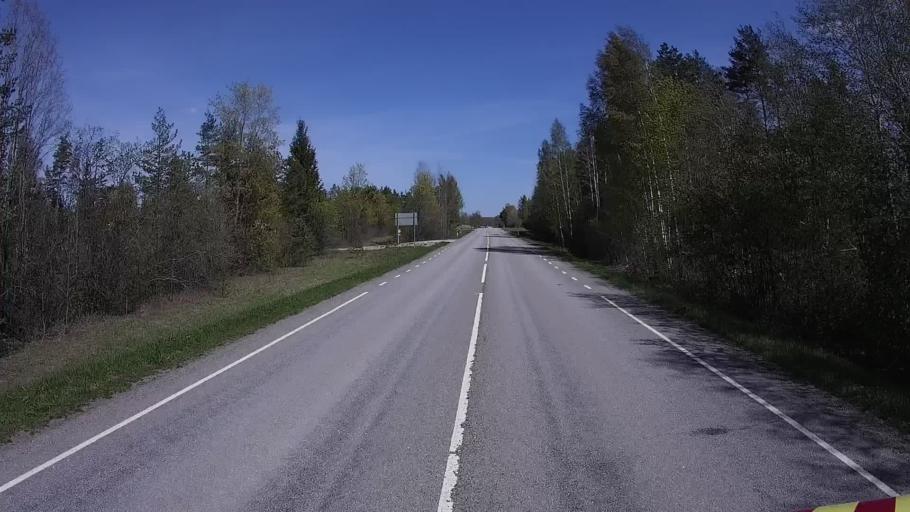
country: EE
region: Laeaene
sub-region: Ridala Parish
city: Uuemoisa
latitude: 58.9611
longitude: 23.6690
